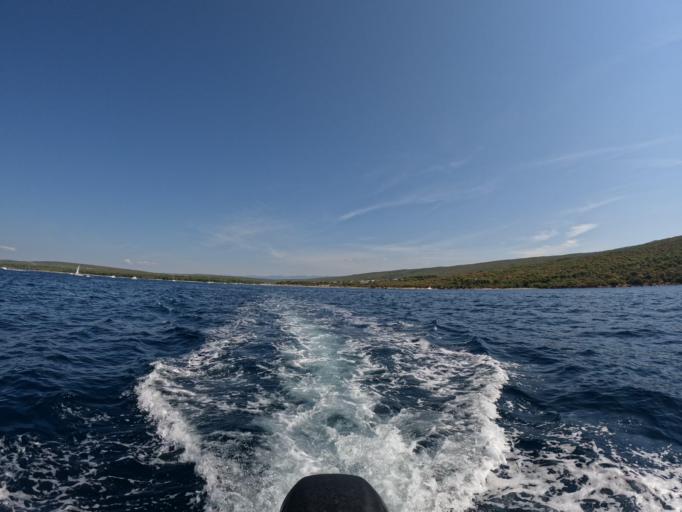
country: HR
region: Primorsko-Goranska
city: Punat
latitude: 45.0000
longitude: 14.6203
